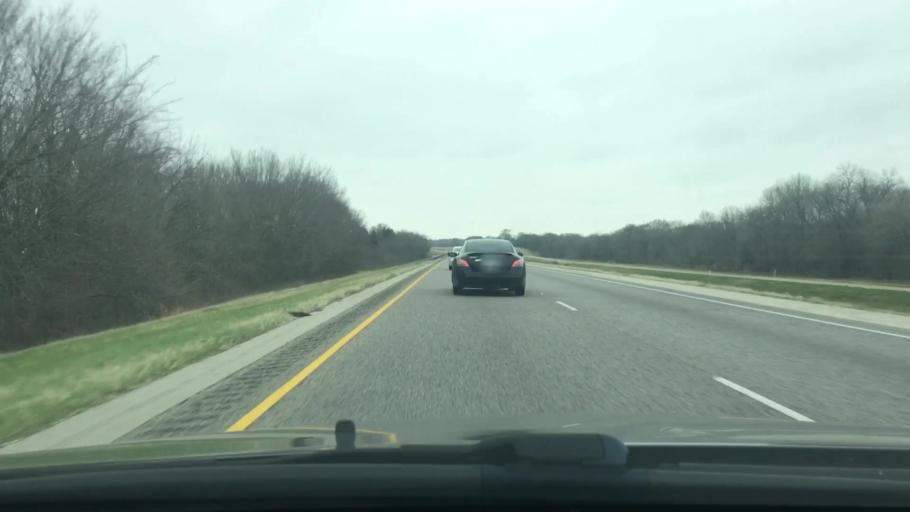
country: US
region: Texas
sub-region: Freestone County
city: Fairfield
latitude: 31.7979
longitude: -96.2559
